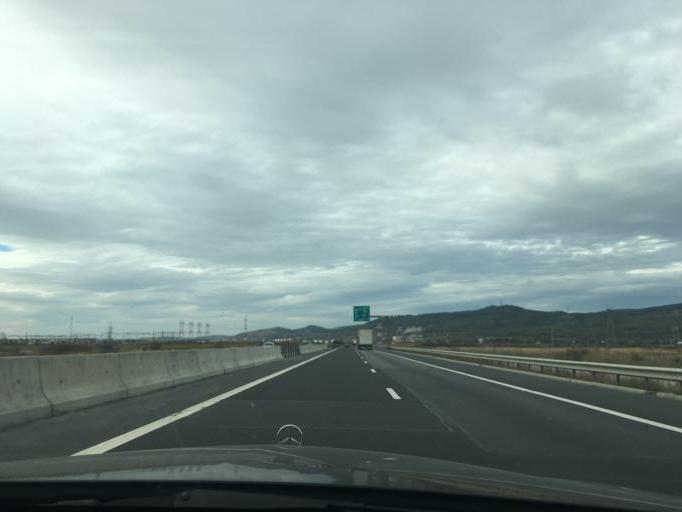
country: RO
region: Sibiu
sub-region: Comuna Selimbar
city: Selimbar
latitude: 45.7774
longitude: 24.2031
